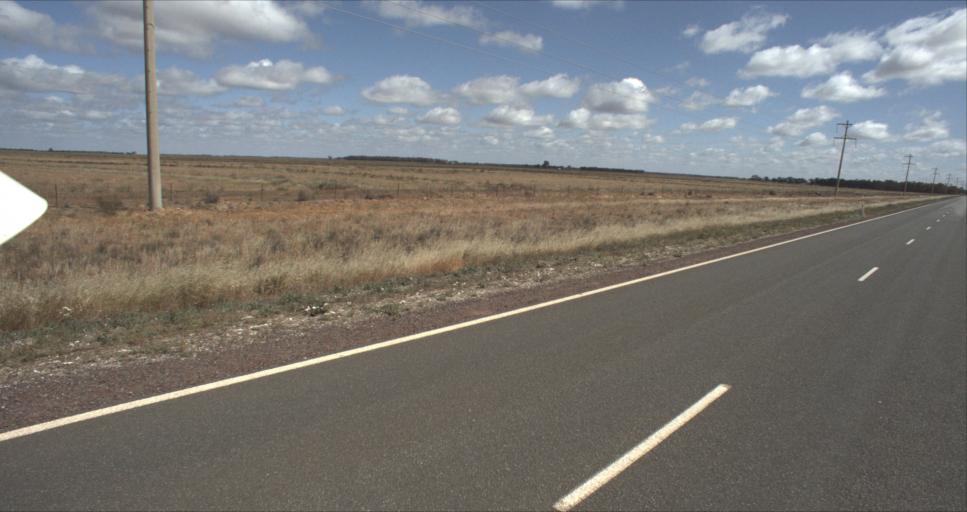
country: AU
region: New South Wales
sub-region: Murrumbidgee Shire
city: Darlington Point
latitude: -34.5858
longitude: 146.1643
